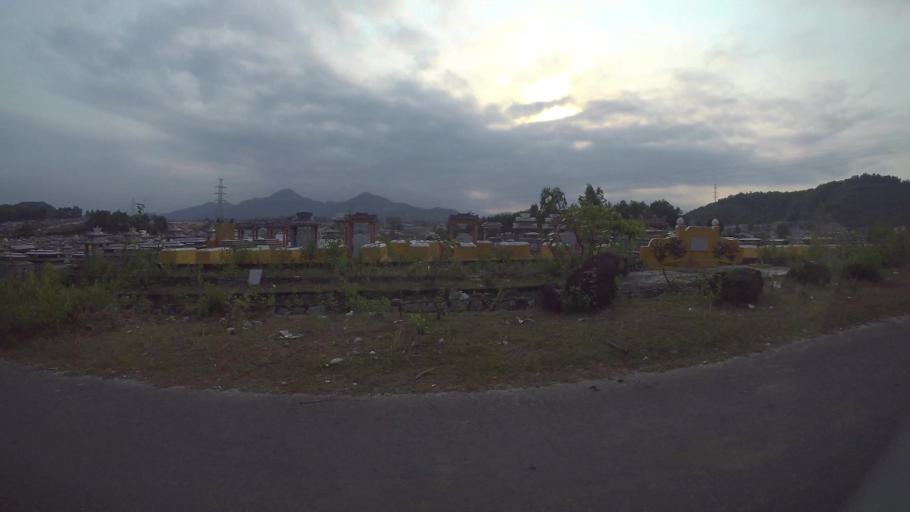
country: VN
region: Da Nang
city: Lien Chieu
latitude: 16.0614
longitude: 108.1118
